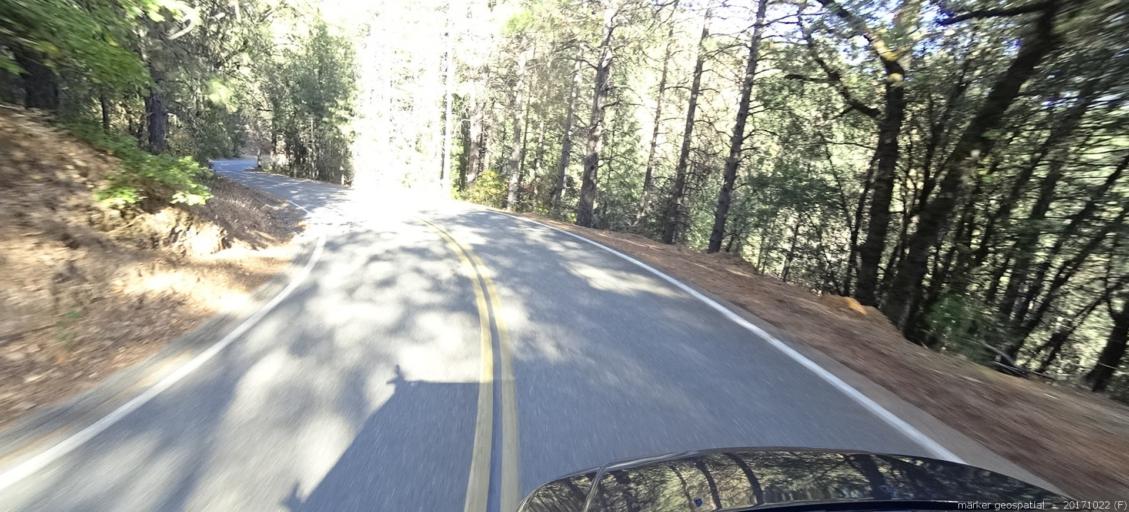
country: US
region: California
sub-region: Shasta County
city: Shasta Lake
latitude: 40.8828
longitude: -122.2754
